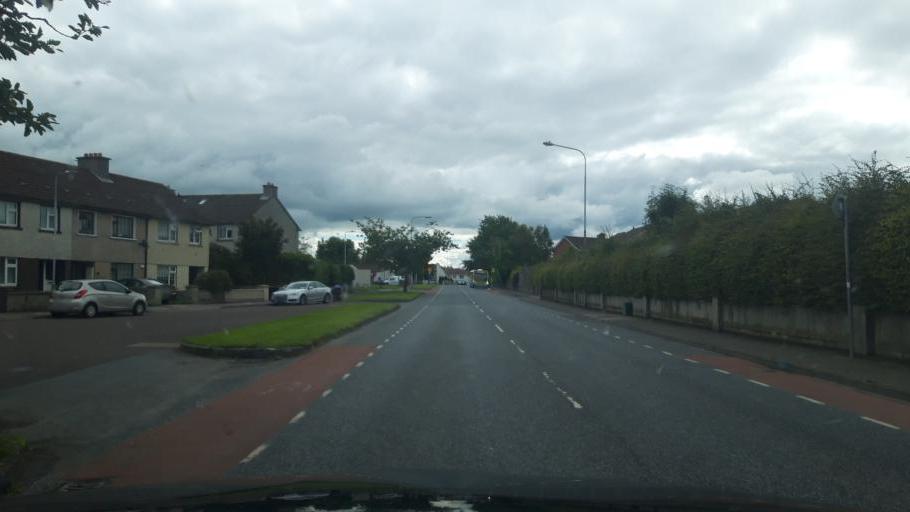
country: IE
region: Leinster
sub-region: Kilkenny
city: Kilkenny
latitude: 52.6411
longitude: -7.2450
